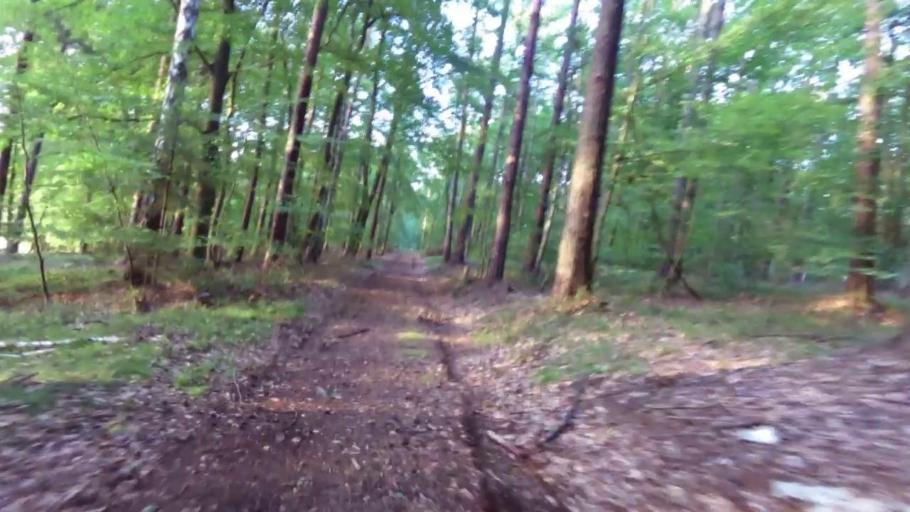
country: PL
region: West Pomeranian Voivodeship
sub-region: Powiat drawski
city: Zlocieniec
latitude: 53.5619
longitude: 16.0185
